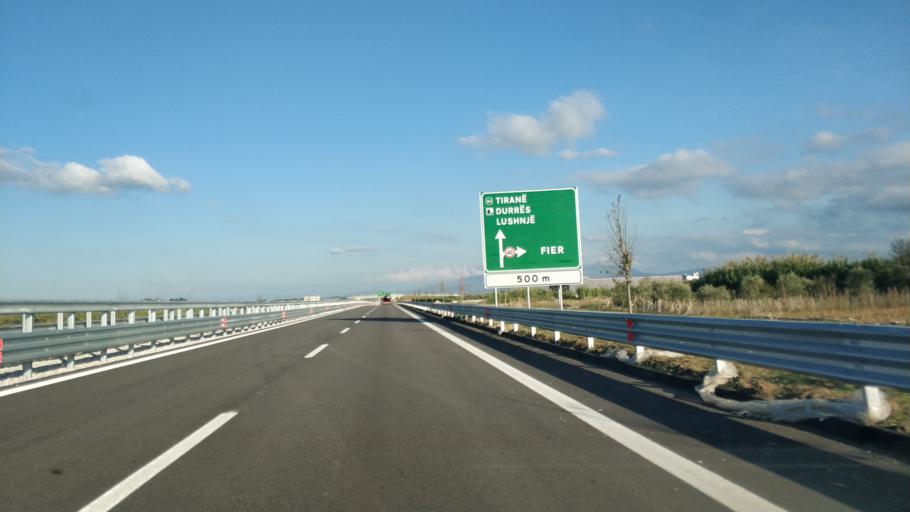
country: AL
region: Fier
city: Fier
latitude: 40.7486
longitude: 19.5455
